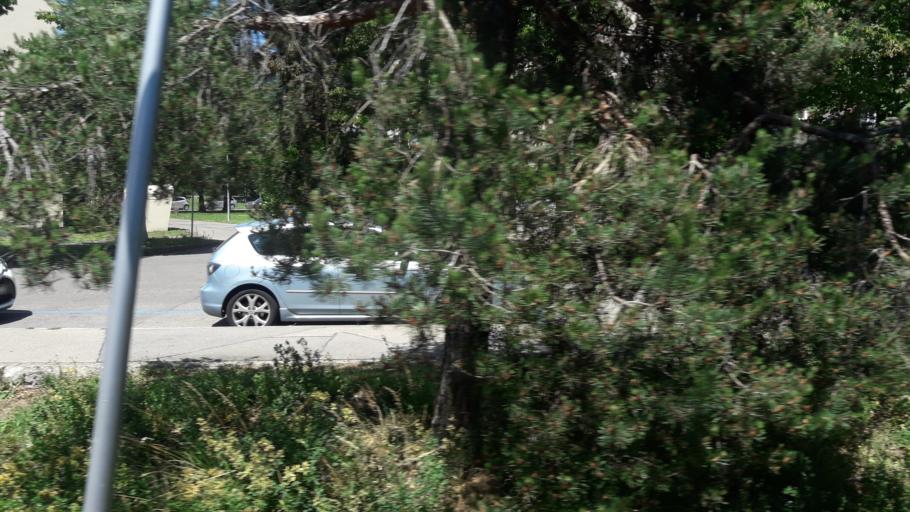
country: CH
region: Bern
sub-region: Biel/Bienne District
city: Nidau
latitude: 47.1198
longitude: 7.2399
